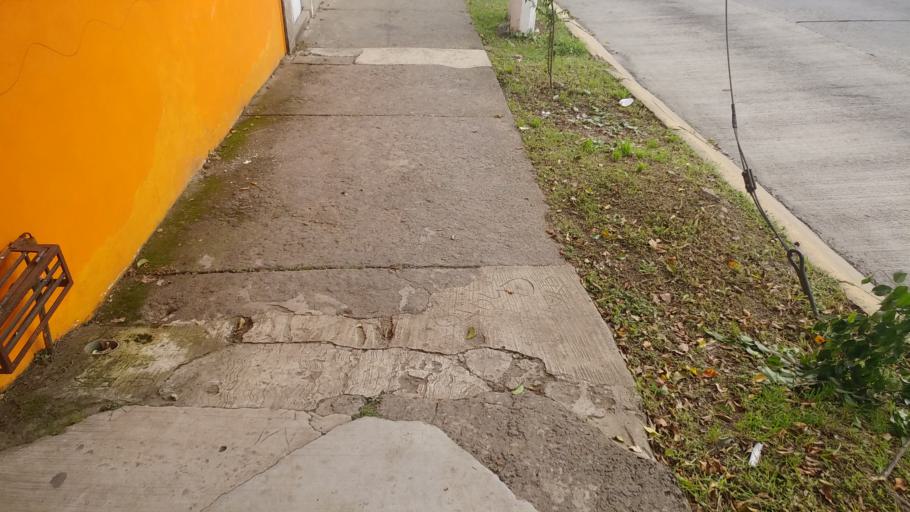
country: MX
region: Veracruz
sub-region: Xalapa
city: Xalapa de Enriquez
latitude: 19.5359
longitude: -96.9182
